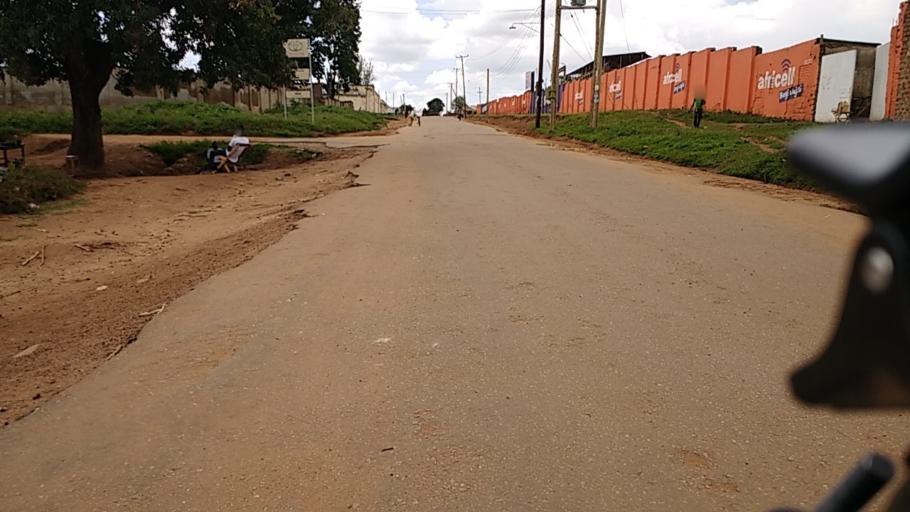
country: UG
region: Eastern Region
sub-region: Mbale District
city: Mbale
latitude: 1.0770
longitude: 34.1650
